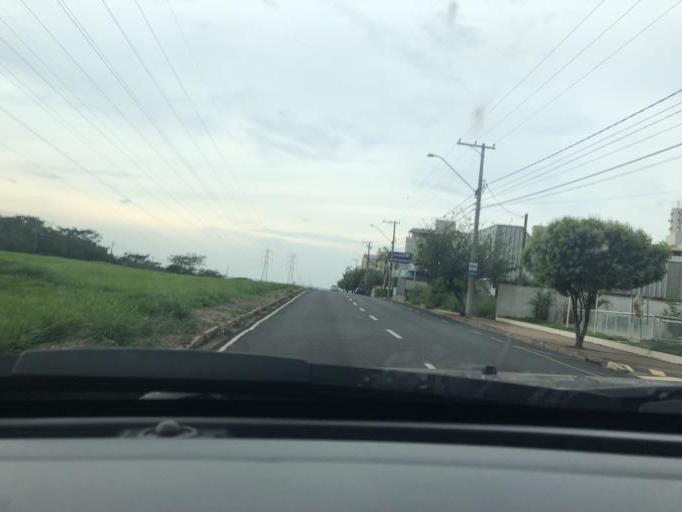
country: BR
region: Sao Paulo
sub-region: Sao Jose Do Rio Preto
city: Sao Jose do Rio Preto
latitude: -20.8445
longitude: -49.3890
